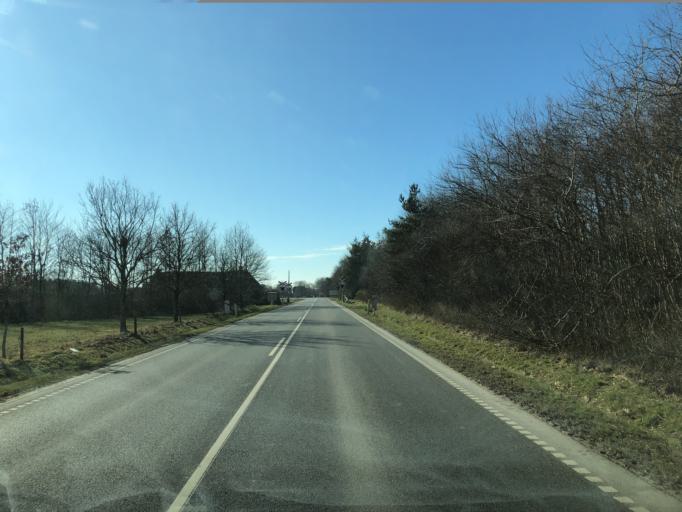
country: DK
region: Central Jutland
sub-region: Ikast-Brande Kommune
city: Bording Kirkeby
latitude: 56.1464
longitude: 9.2189
